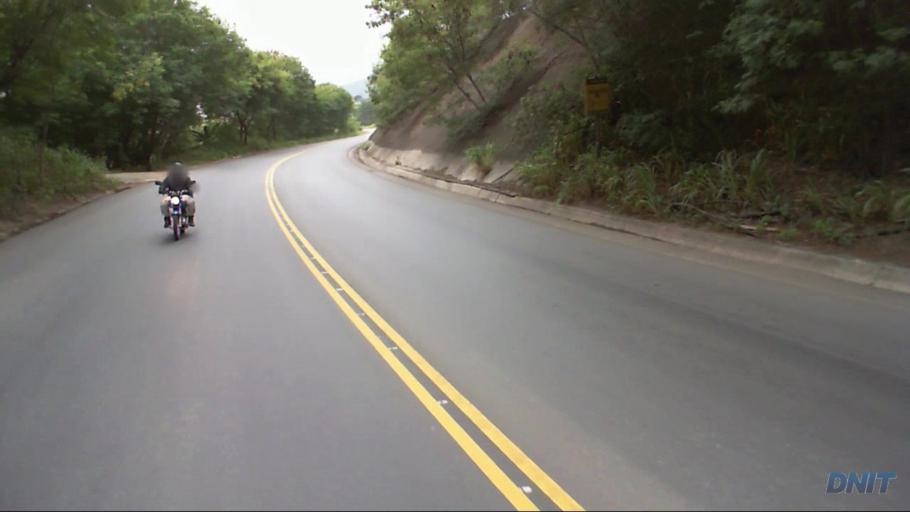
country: BR
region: Minas Gerais
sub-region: Coronel Fabriciano
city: Coronel Fabriciano
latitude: -19.5236
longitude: -42.6505
